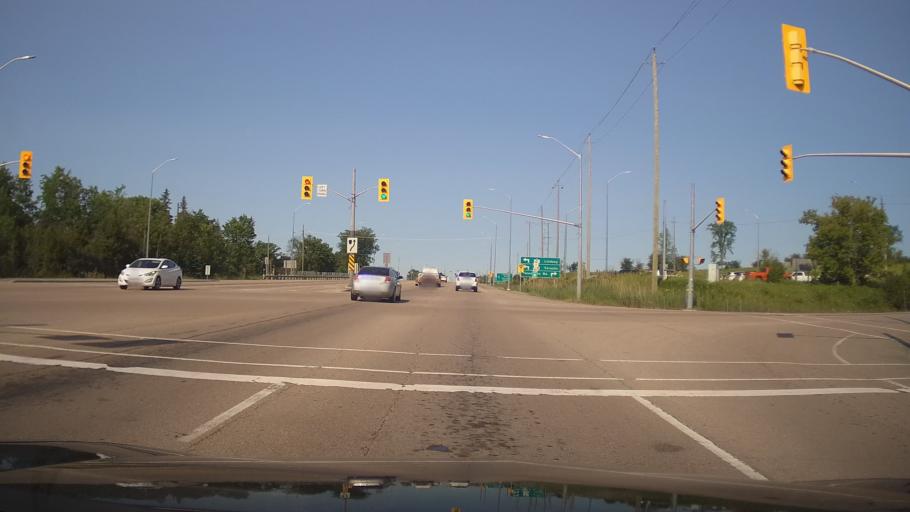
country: CA
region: Ontario
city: Peterborough
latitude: 44.2953
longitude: -78.2771
